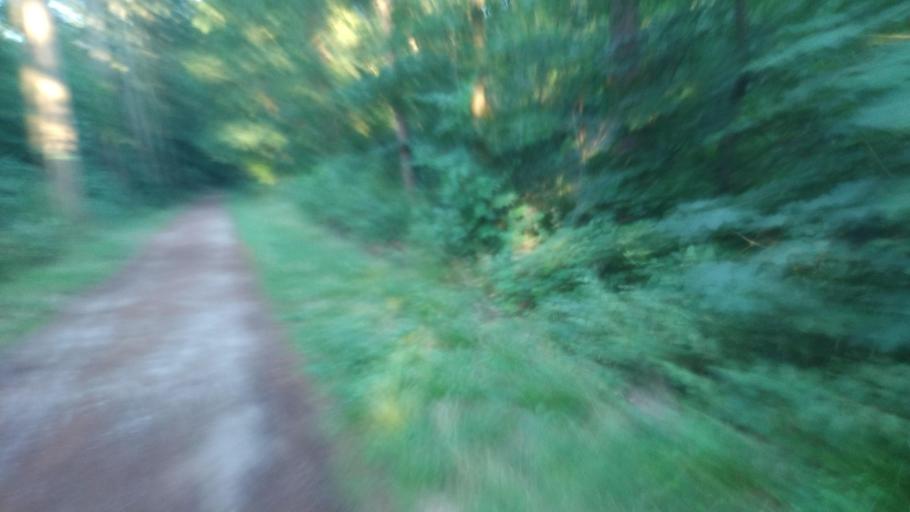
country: DE
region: Baden-Wuerttemberg
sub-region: Karlsruhe Region
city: Bruchsal
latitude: 49.1093
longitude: 8.5628
